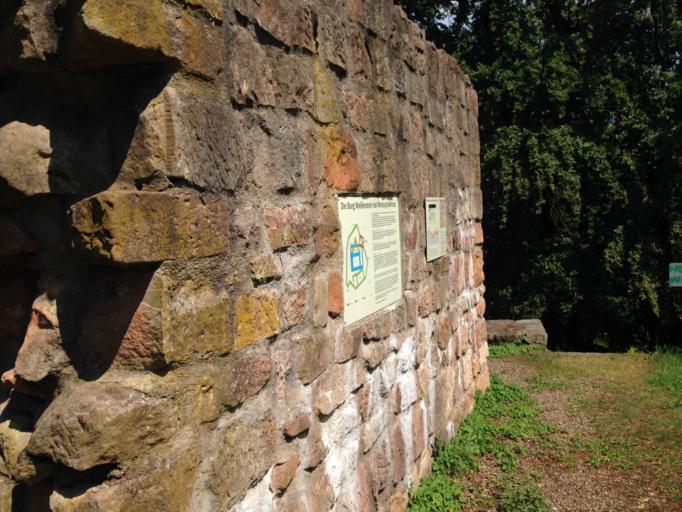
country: DE
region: Hesse
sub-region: Regierungsbezirk Giessen
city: Marburg an der Lahn
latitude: 50.8490
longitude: 8.7546
